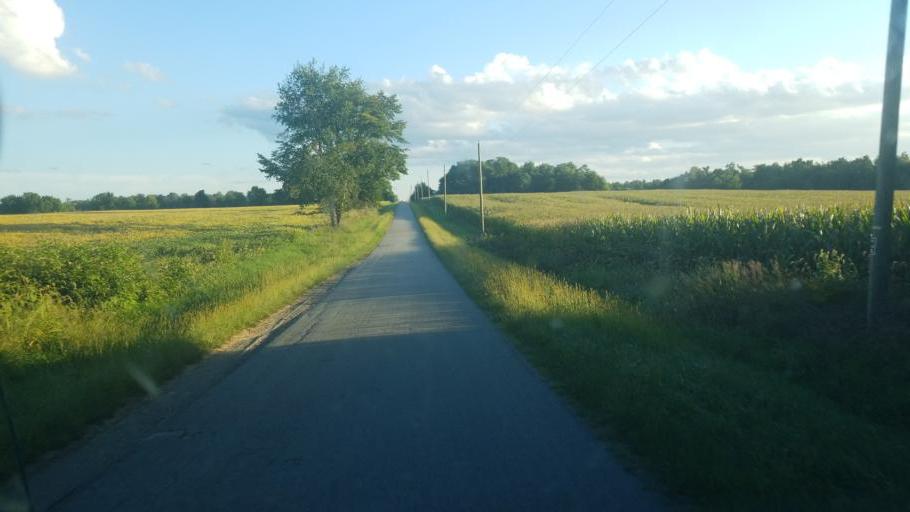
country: US
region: Ohio
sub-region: Wyandot County
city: Upper Sandusky
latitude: 40.8552
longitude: -83.1507
